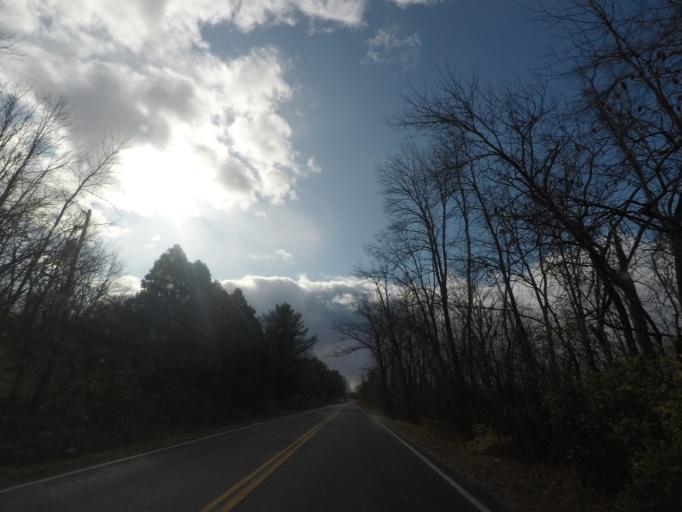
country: US
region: New York
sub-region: Saratoga County
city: Ballston Spa
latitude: 42.9582
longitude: -73.8445
